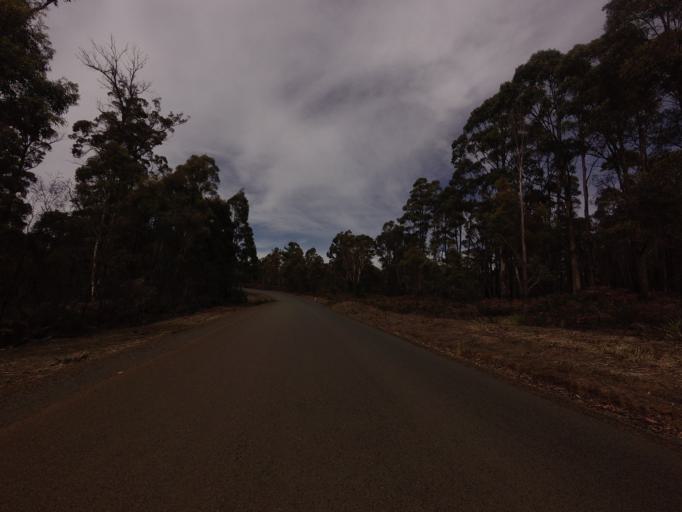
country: AU
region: Tasmania
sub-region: Sorell
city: Sorell
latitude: -42.5135
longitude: 147.6436
